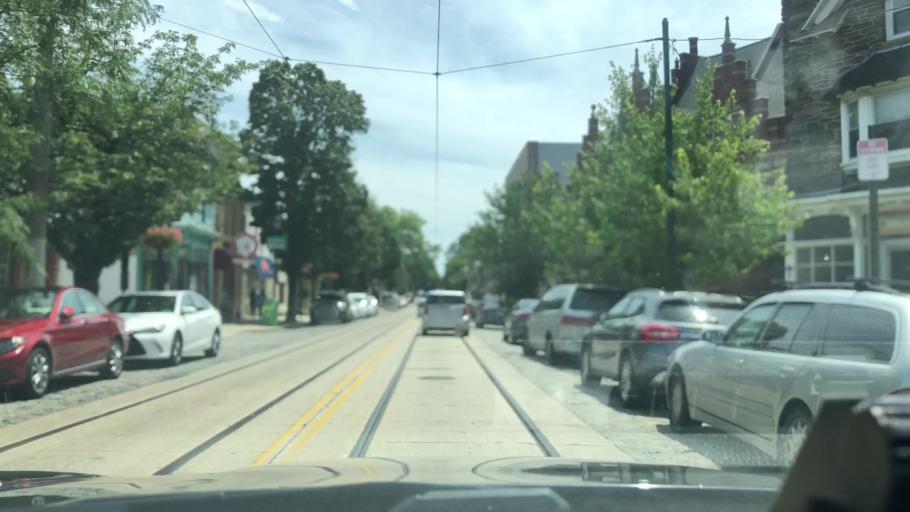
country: US
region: Pennsylvania
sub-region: Montgomery County
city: Wyndmoor
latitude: 40.0516
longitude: -75.1853
